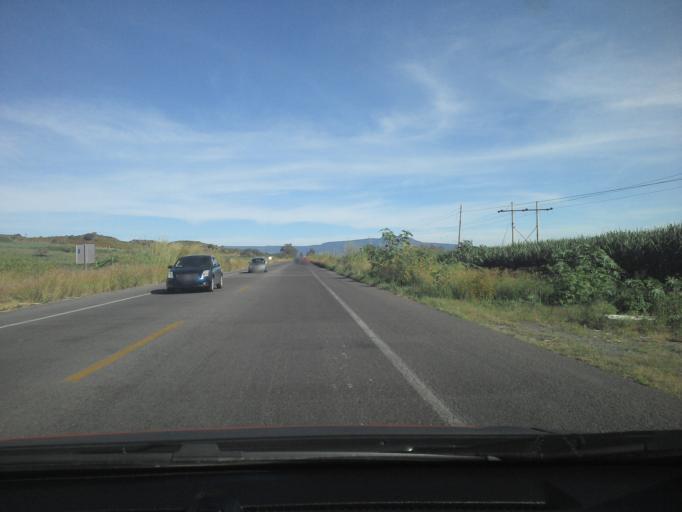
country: MX
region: Jalisco
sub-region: Teuchitlan
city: La Estanzuela
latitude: 20.6686
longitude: -103.7985
